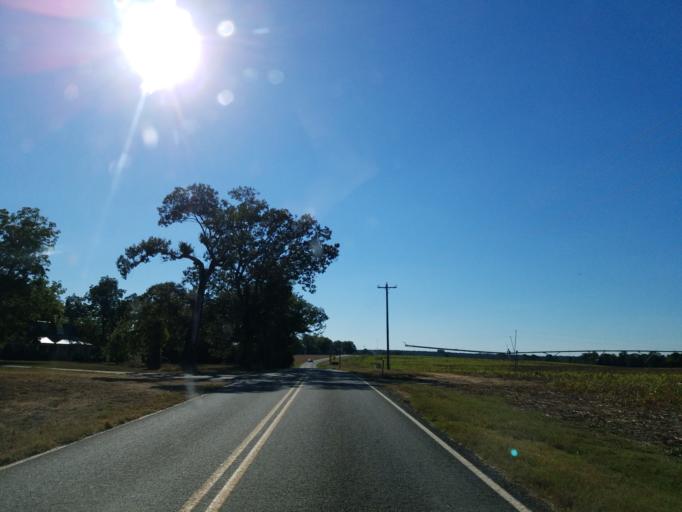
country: US
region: Georgia
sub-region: Dooly County
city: Unadilla
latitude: 32.2448
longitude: -83.8238
